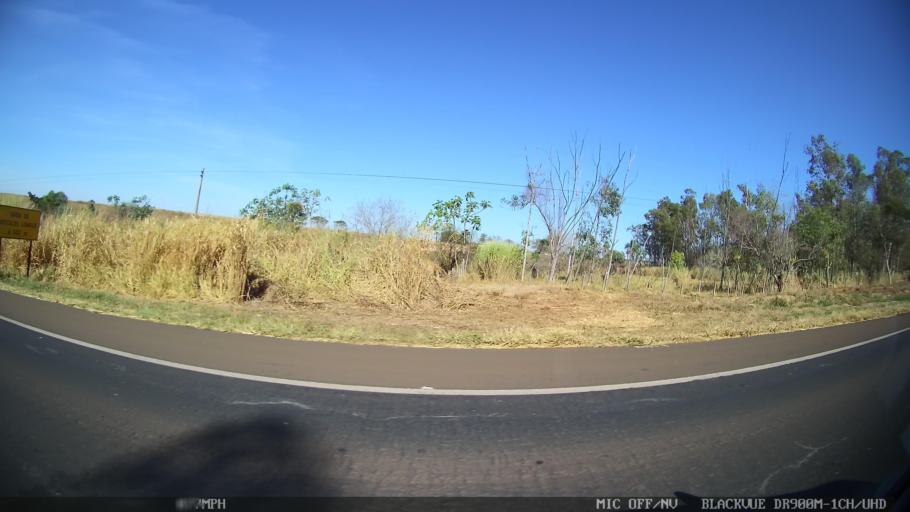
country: BR
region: Sao Paulo
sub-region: Olimpia
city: Olimpia
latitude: -20.6406
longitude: -48.8270
